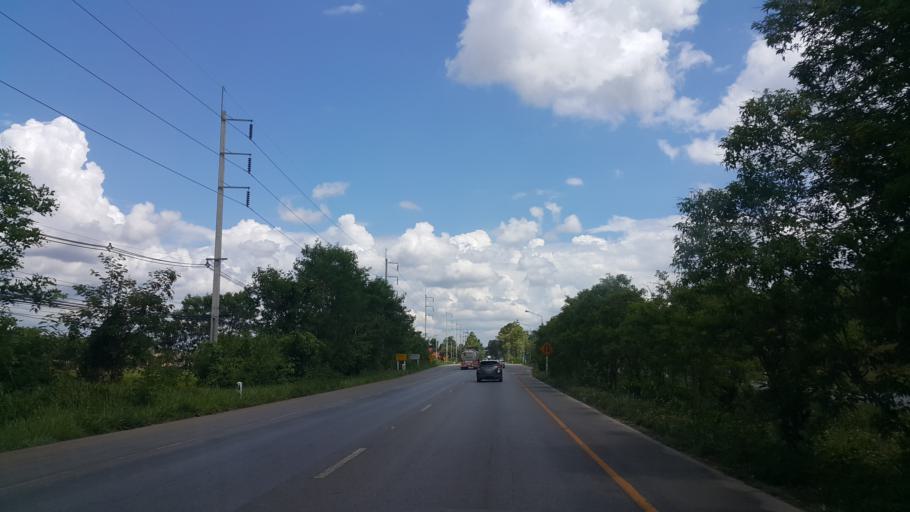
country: TH
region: Phayao
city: Dok Kham Tai
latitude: 19.0593
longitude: 99.9309
